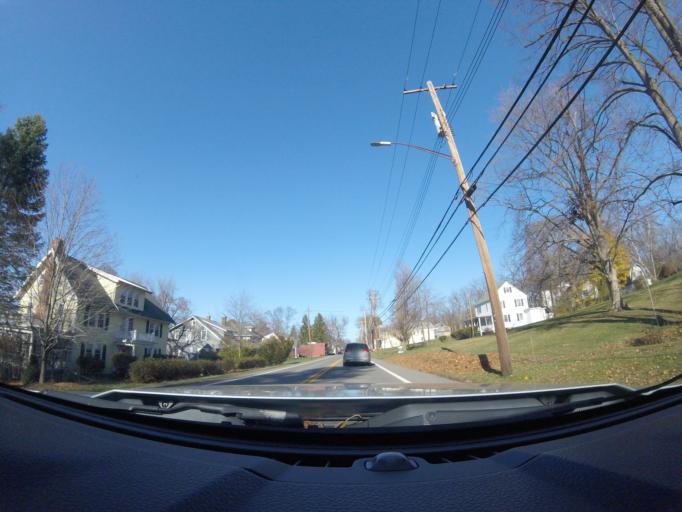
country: US
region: New York
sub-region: Cayuga County
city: Union Springs
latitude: 42.7484
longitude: -76.7006
